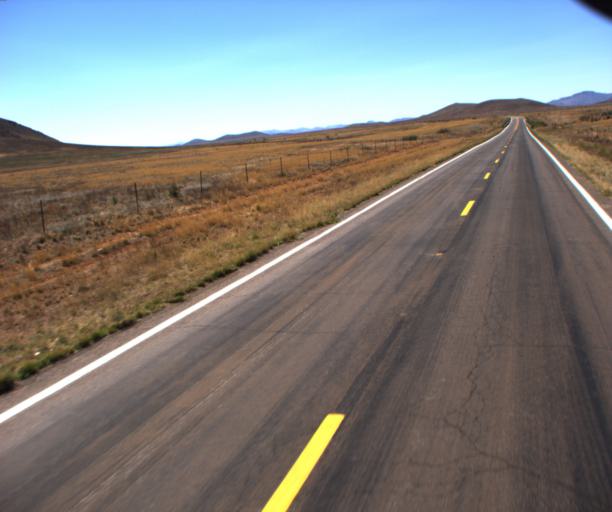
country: US
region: Arizona
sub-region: Cochise County
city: Douglas
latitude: 31.5843
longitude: -109.2500
